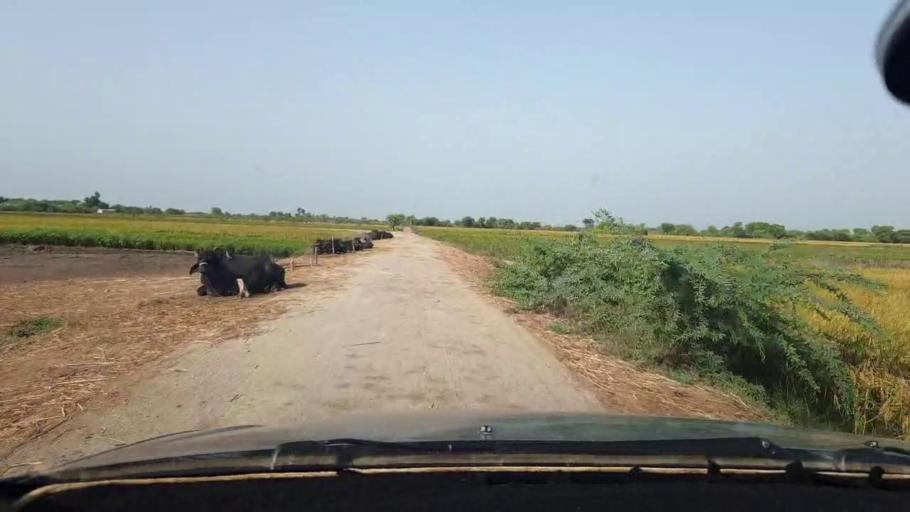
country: PK
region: Sindh
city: Tando Bago
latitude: 24.8210
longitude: 68.8994
